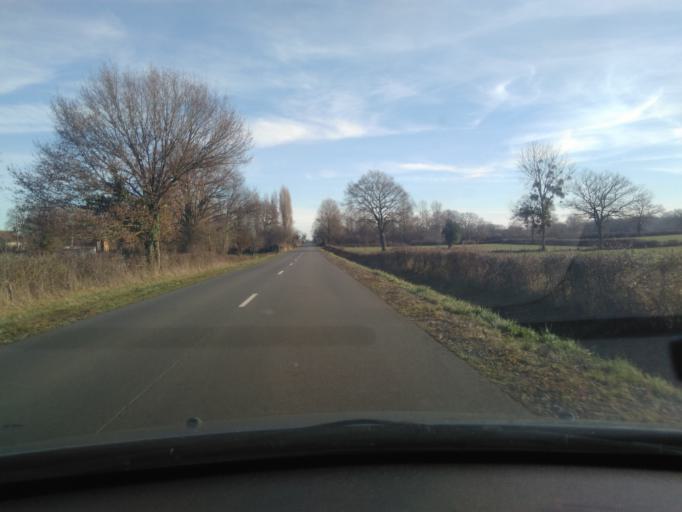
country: FR
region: Centre
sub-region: Departement du Cher
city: Orval
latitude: 46.6539
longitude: 2.4061
